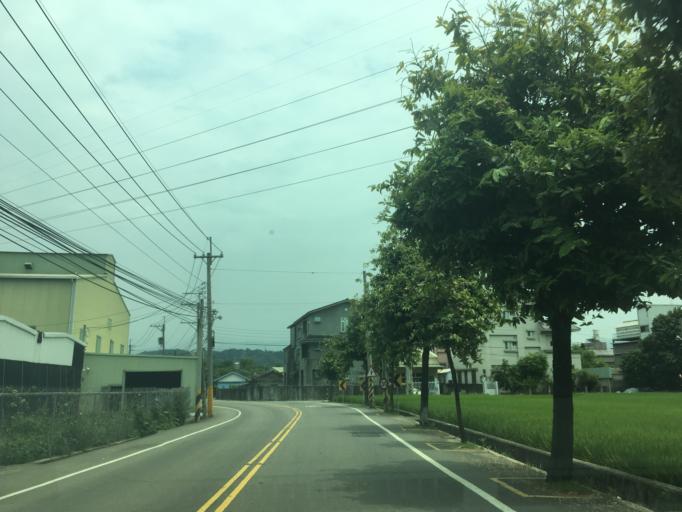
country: TW
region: Taiwan
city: Zhongxing New Village
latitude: 24.0499
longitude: 120.6821
